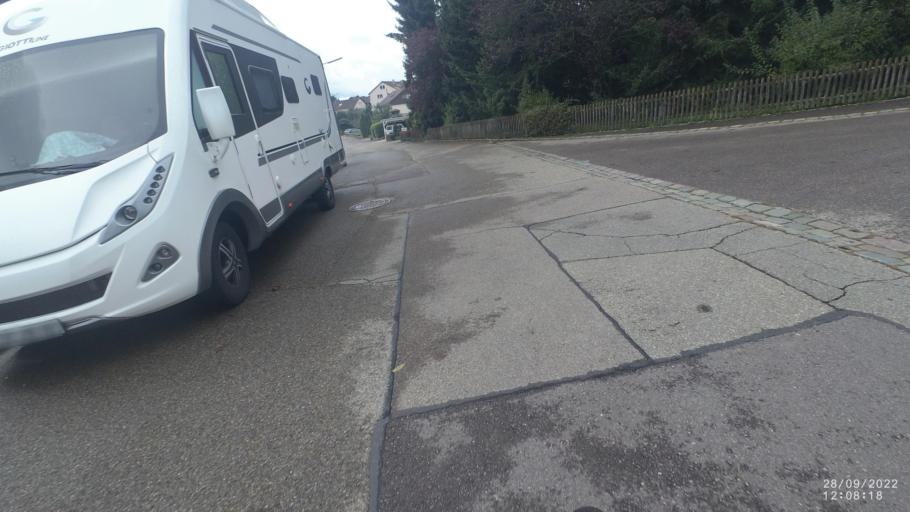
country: DE
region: Baden-Wuerttemberg
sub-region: Regierungsbezirk Stuttgart
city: Wangen
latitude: 48.7280
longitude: 9.6130
